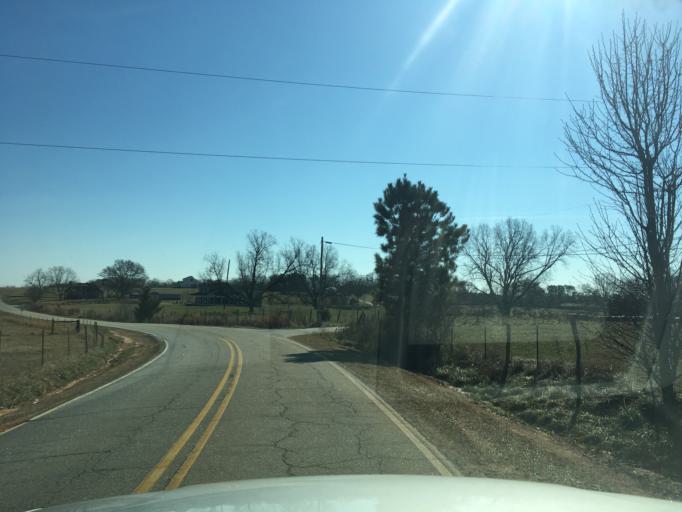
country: US
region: South Carolina
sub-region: Pickens County
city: Liberty
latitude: 34.8205
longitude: -82.7802
